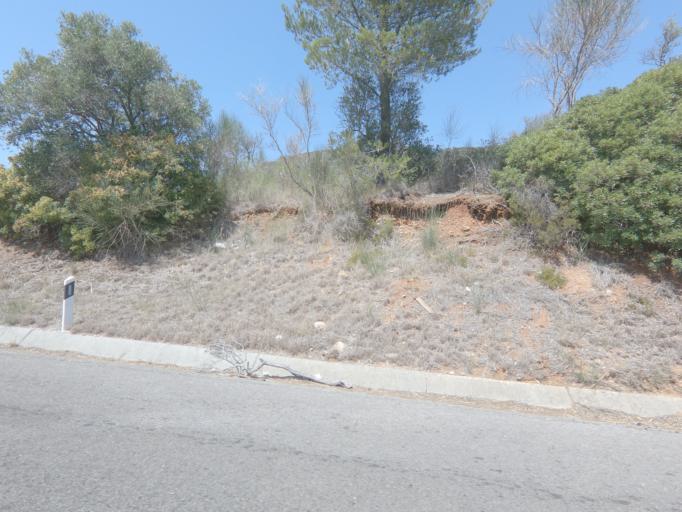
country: PT
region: Setubal
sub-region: Palmela
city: Quinta do Anjo
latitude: 38.5251
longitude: -8.9387
